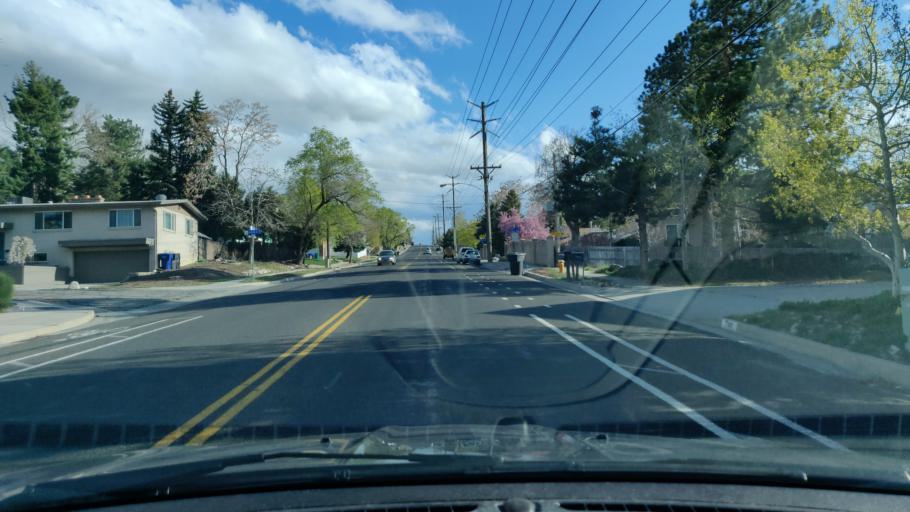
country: US
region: Utah
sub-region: Salt Lake County
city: Cottonwood Heights
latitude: 40.6208
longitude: -111.8248
